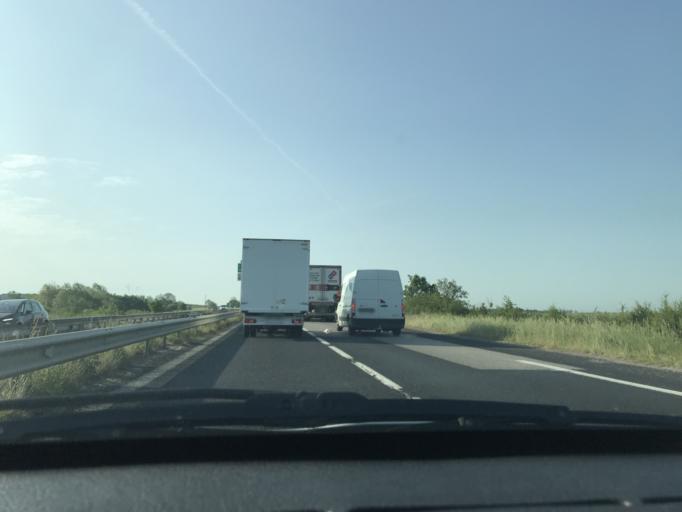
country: FR
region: Lorraine
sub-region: Departement de Meurthe-et-Moselle
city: Flavigny-sur-Moselle
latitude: 48.5550
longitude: 6.1879
